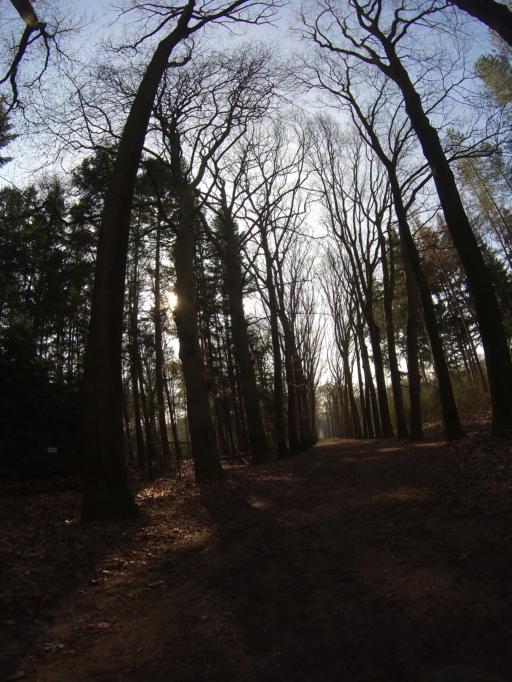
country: NL
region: Utrecht
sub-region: Gemeente Amersfoort
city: Randenbroek
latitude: 52.1370
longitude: 5.3897
